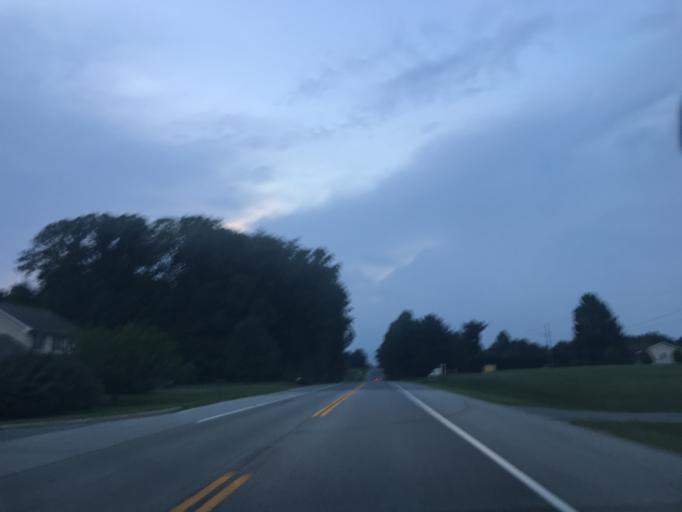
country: US
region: Maryland
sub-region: Cecil County
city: Rising Sun
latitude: 39.6820
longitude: -76.0751
